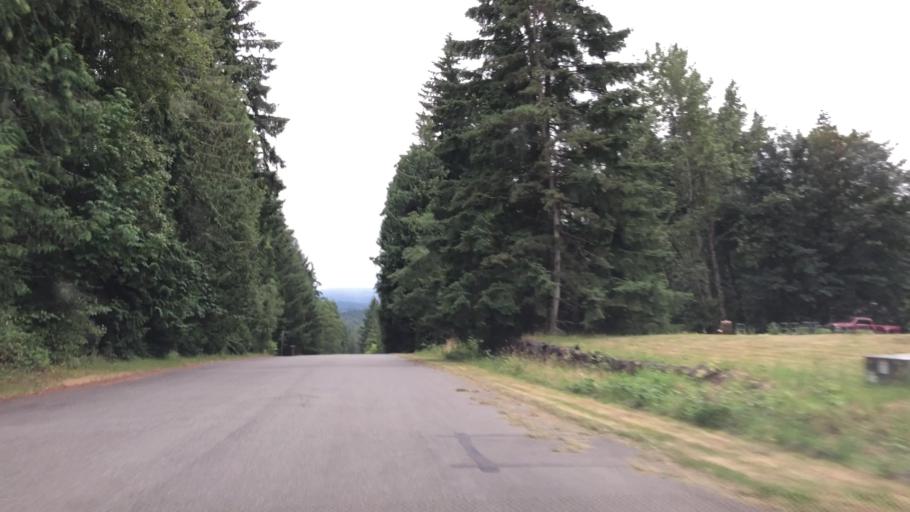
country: US
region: Washington
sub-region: King County
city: Cottage Lake
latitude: 47.7224
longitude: -122.0941
